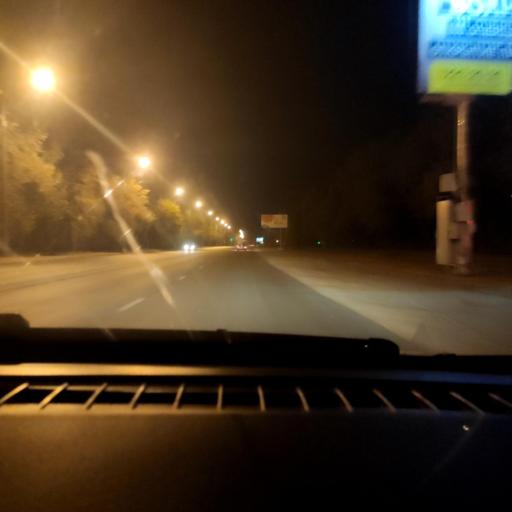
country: RU
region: Voronezj
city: Voronezh
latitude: 51.6391
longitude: 39.2649
